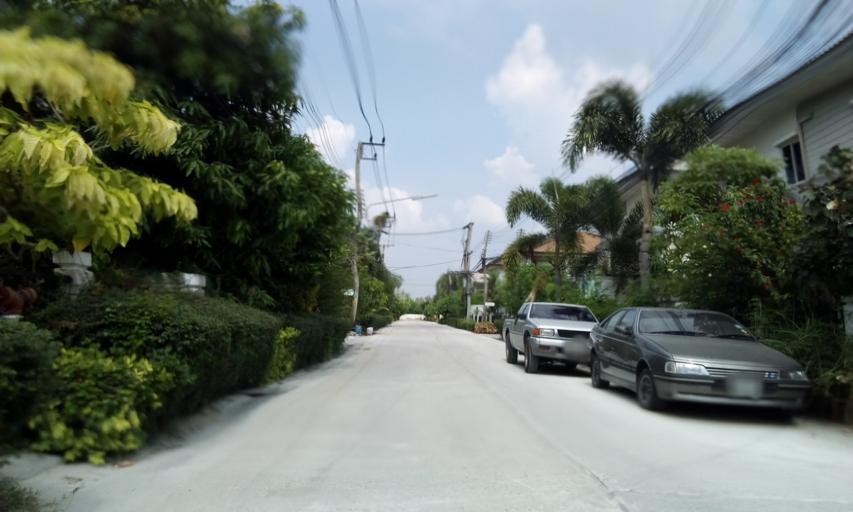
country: TH
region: Pathum Thani
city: Ban Rangsit
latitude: 14.0463
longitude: 100.7652
